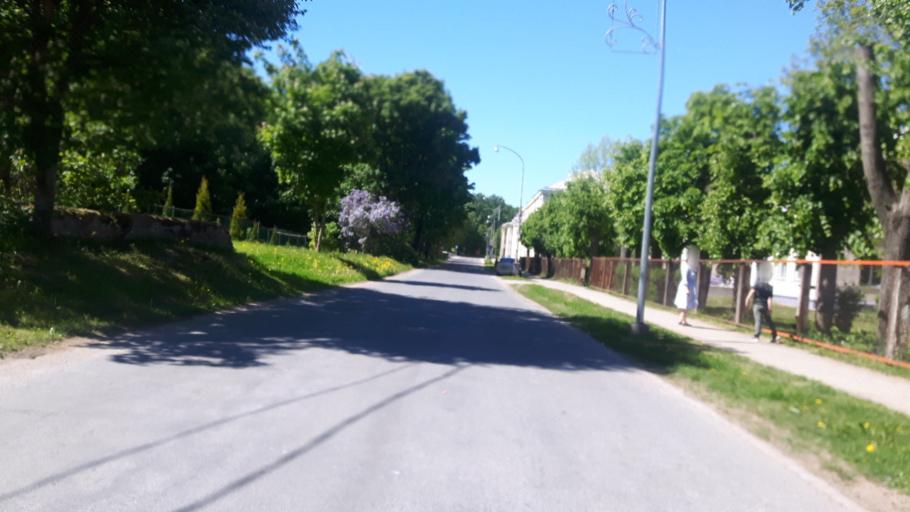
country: EE
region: Ida-Virumaa
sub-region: Sillamaee linn
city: Sillamae
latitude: 59.3966
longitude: 27.7667
